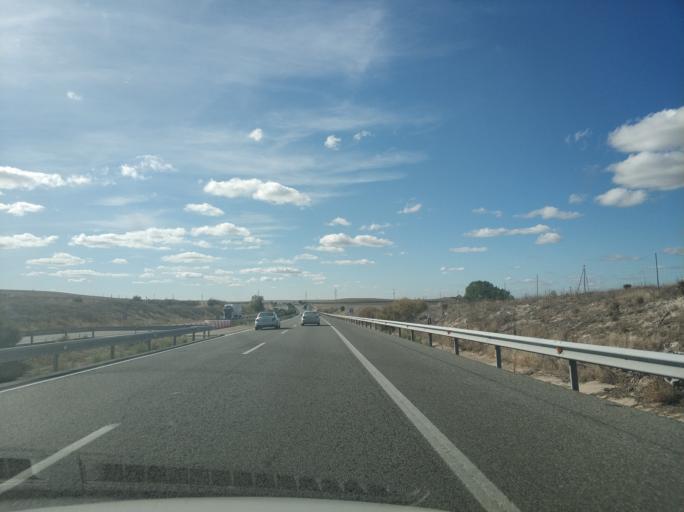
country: ES
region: Castille and Leon
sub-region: Provincia de Burgos
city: Albillos
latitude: 42.3063
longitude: -3.7845
